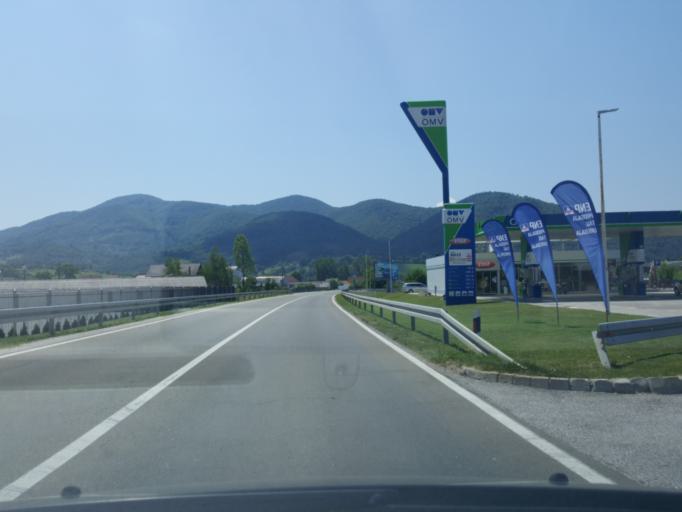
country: RS
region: Central Serbia
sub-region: Moravicki Okrug
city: Gornji Milanovac
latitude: 44.0117
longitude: 20.4633
